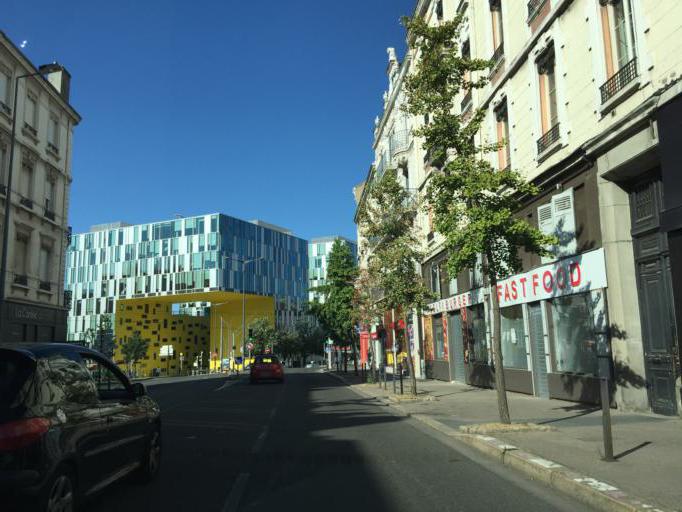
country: FR
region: Rhone-Alpes
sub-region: Departement de la Loire
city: Saint-Etienne
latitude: 45.4391
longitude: 4.3973
